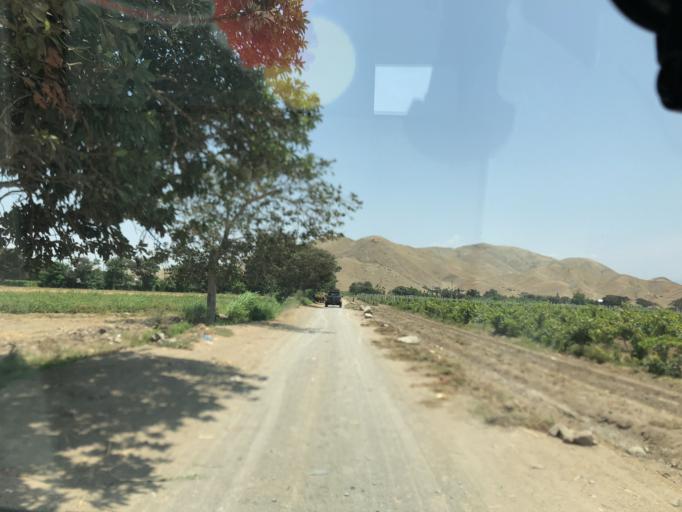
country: PE
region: Lima
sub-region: Provincia de Canete
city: Quilmana
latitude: -12.9686
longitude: -76.4161
